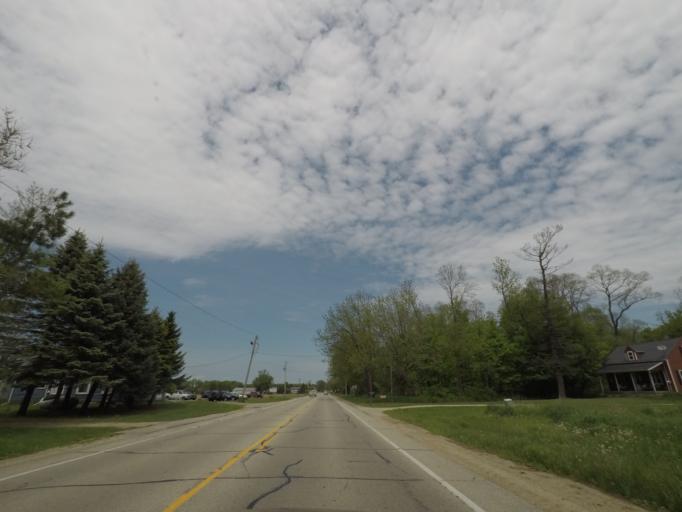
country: US
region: Wisconsin
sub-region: Rock County
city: Evansville
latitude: 42.8214
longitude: -89.3010
